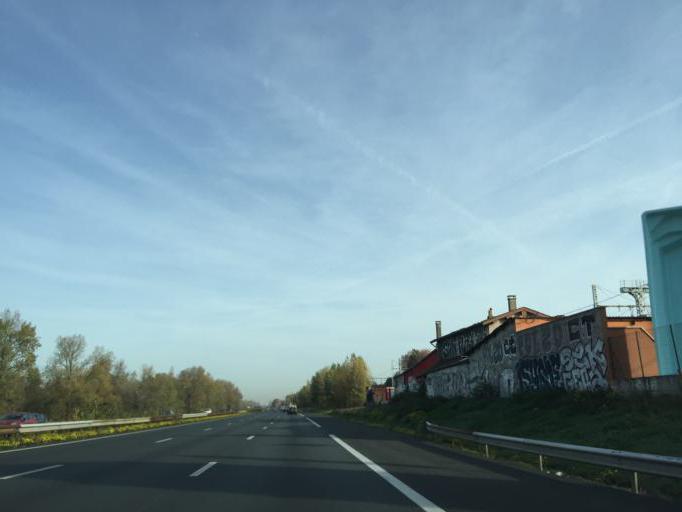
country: FR
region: Rhone-Alpes
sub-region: Departement du Rhone
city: Ternay
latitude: 45.6176
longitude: 4.8116
